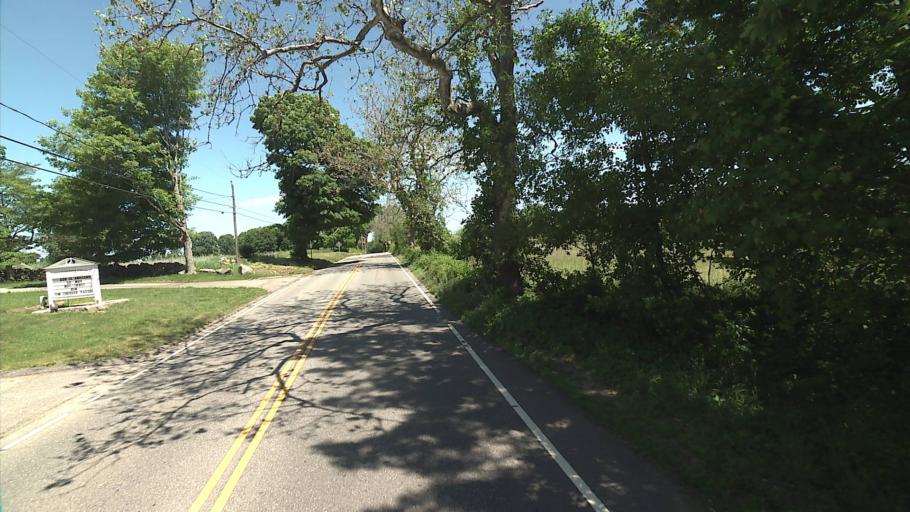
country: US
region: Rhode Island
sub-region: Washington County
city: Hopkinton
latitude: 41.5055
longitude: -71.8391
